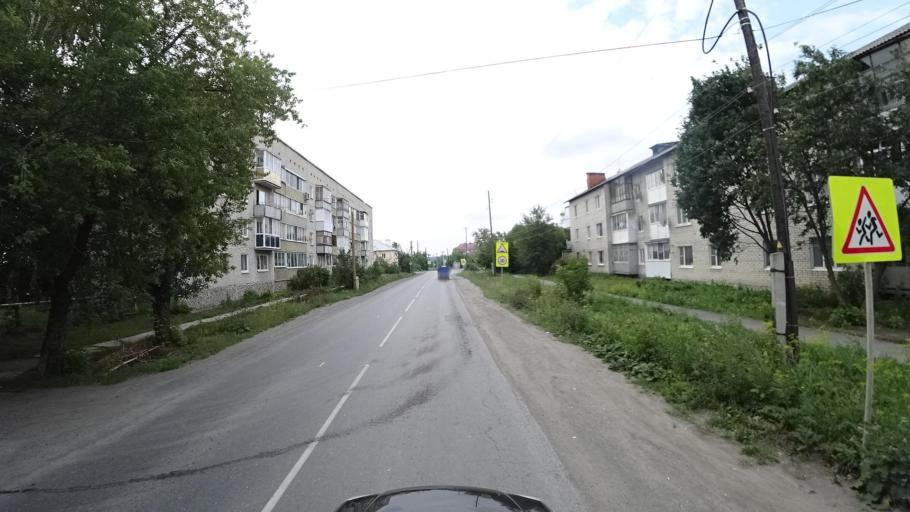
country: RU
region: Sverdlovsk
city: Kamyshlov
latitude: 56.8479
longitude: 62.6919
